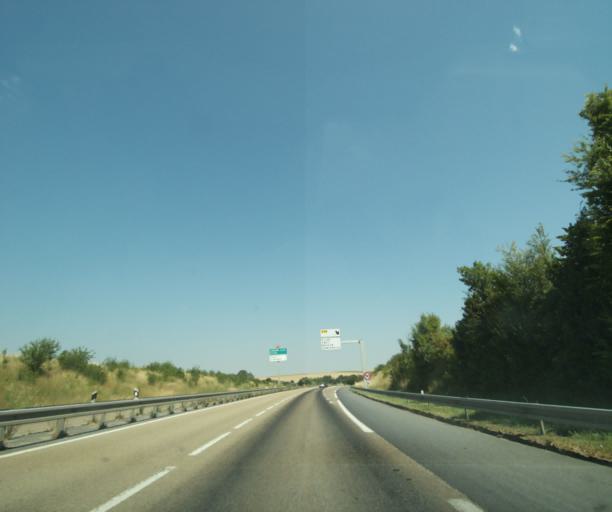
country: FR
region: Champagne-Ardenne
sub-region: Departement de la Marne
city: Sarry
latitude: 48.8582
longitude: 4.4894
